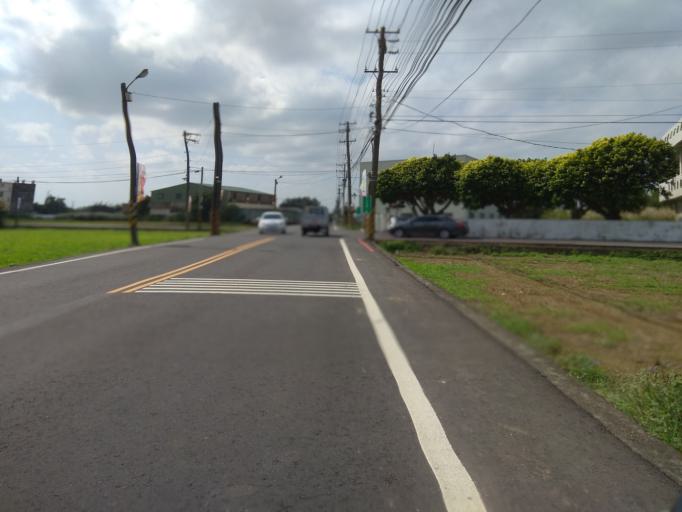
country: TW
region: Taiwan
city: Taoyuan City
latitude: 25.0715
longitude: 121.2476
